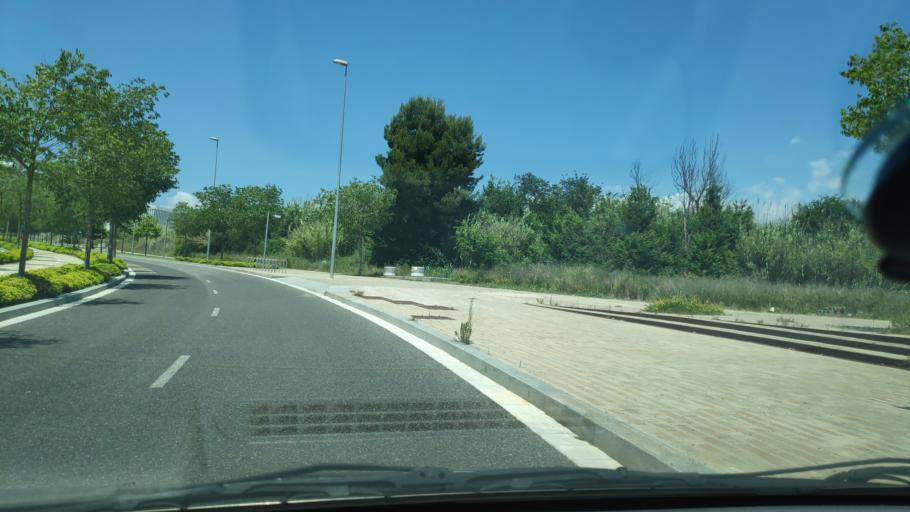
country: ES
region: Catalonia
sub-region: Provincia de Barcelona
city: Cerdanyola del Valles
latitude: 41.4869
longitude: 2.1148
